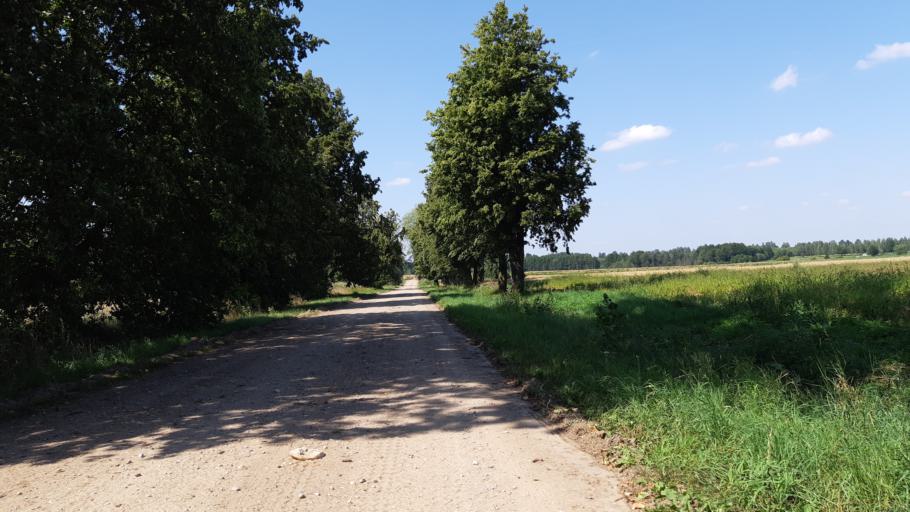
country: LT
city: Virbalis
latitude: 54.6375
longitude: 22.8234
